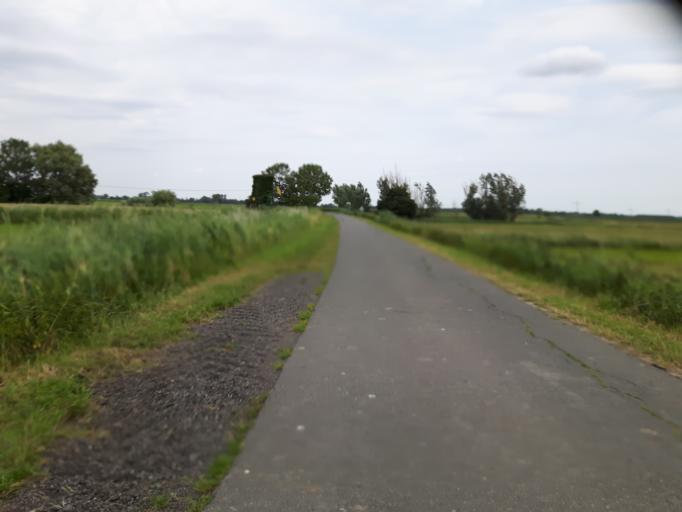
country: DE
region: Lower Saxony
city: Varel
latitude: 53.3716
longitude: 8.2099
